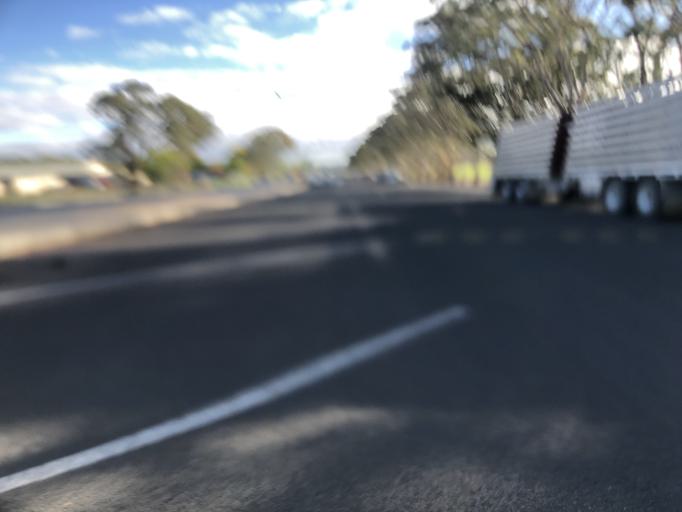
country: AU
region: New South Wales
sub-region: Orange Municipality
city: Orange
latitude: -33.3091
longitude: 149.0969
